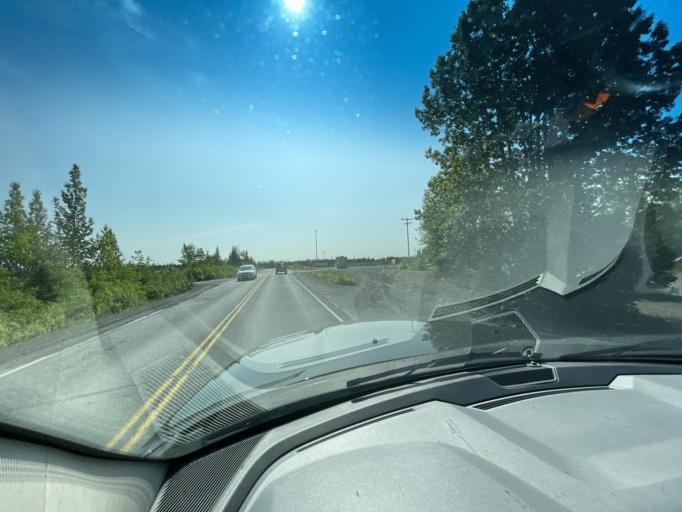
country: US
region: Alaska
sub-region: Kenai Peninsula Borough
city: Cohoe
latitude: 60.2989
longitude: -151.2803
